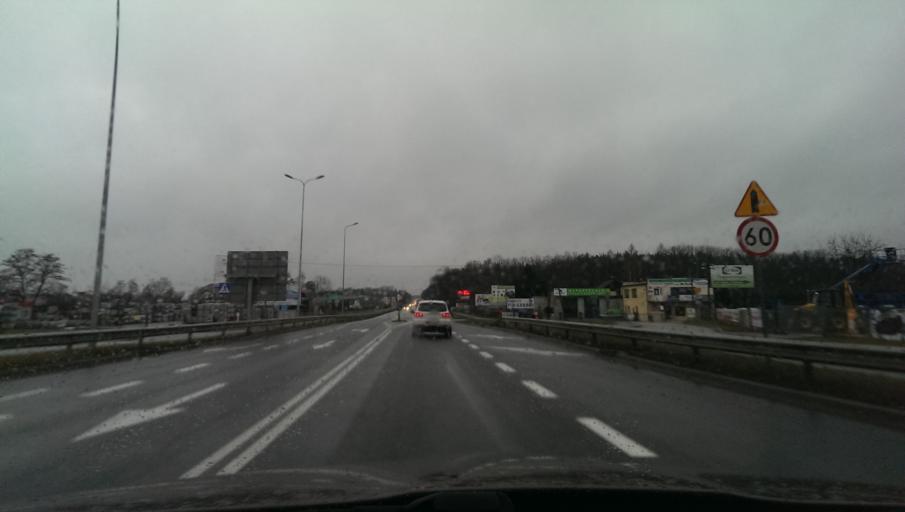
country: PL
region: Subcarpathian Voivodeship
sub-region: Powiat rzeszowski
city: Rudna Mala
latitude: 50.1165
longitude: 21.9724
